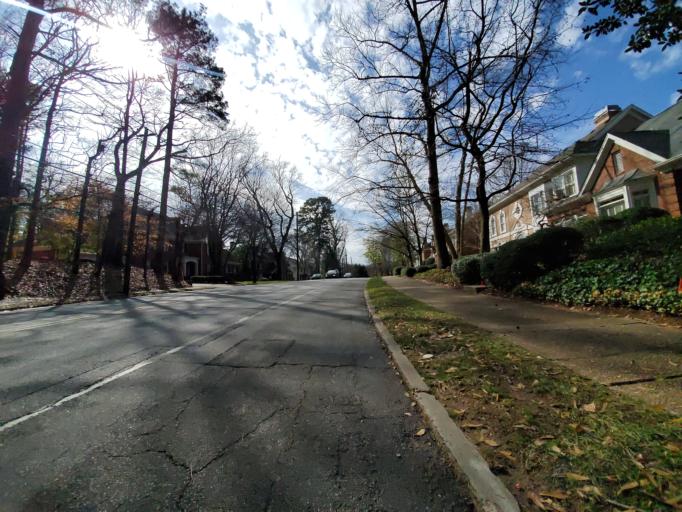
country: US
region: Georgia
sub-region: DeKalb County
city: Druid Hills
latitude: 33.7727
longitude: -84.3319
